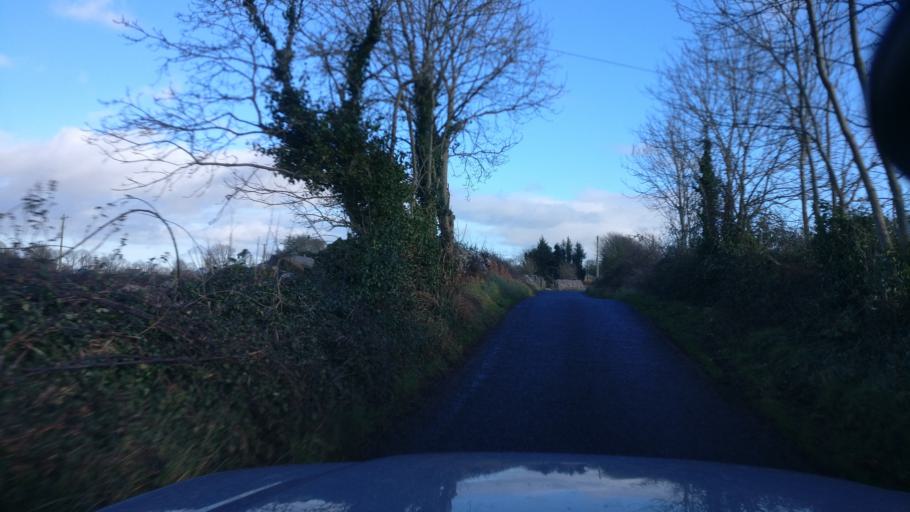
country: IE
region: Connaught
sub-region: County Galway
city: Loughrea
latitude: 53.2307
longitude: -8.5848
